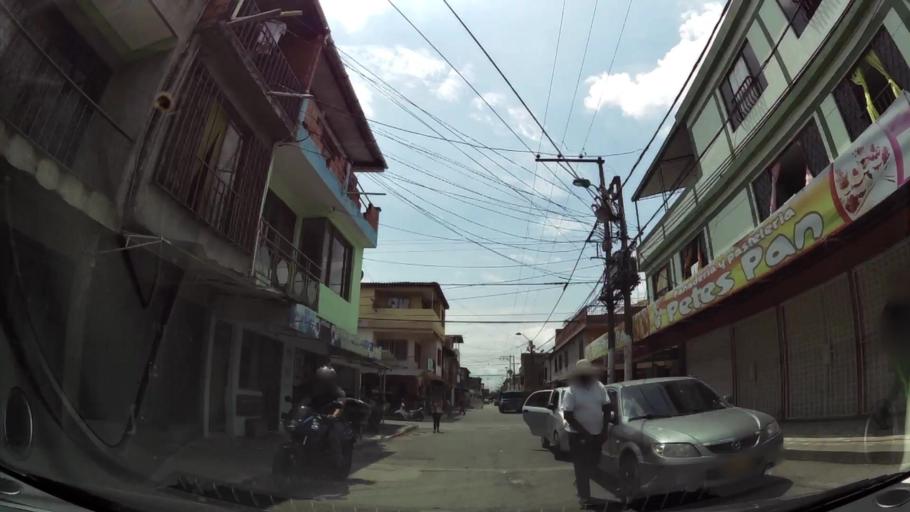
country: CO
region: Valle del Cauca
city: Cali
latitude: 3.4758
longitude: -76.4806
